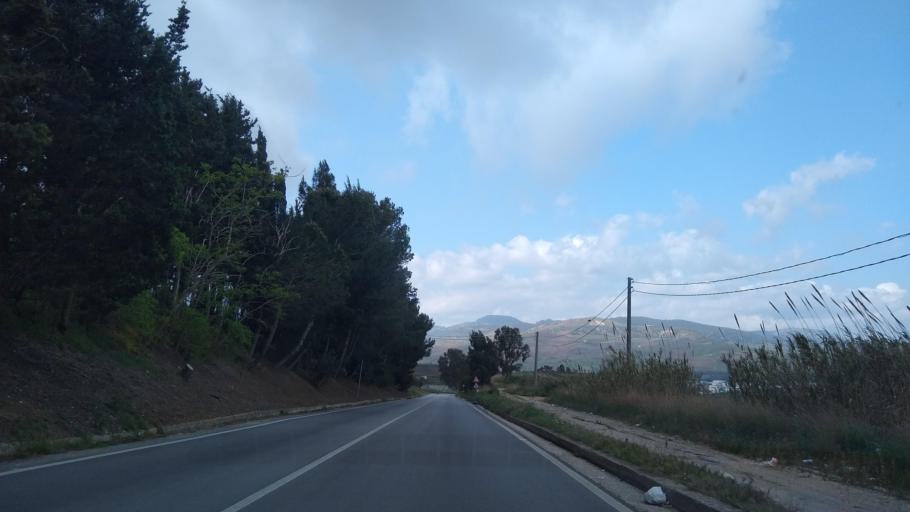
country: IT
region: Sicily
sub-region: Trapani
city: Alcamo
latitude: 37.9729
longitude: 12.9343
